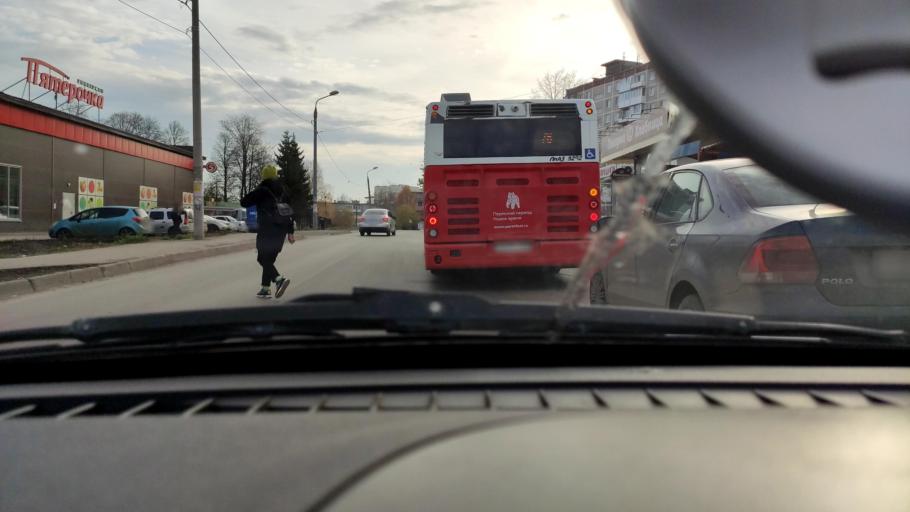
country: RU
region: Perm
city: Perm
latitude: 58.0886
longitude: 56.4018
